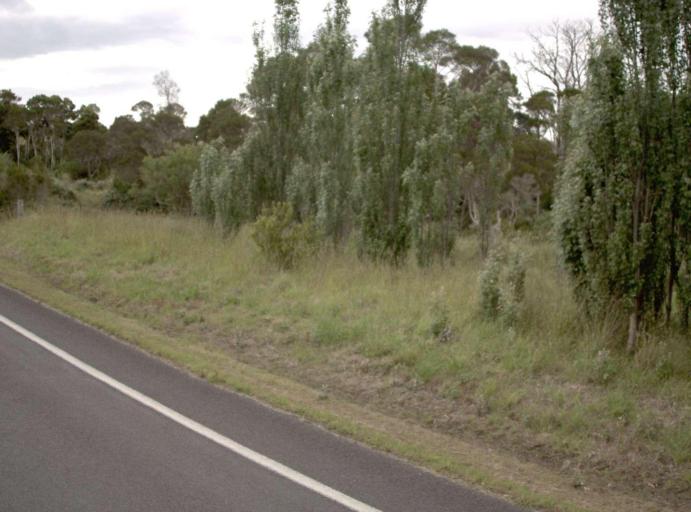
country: AU
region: Victoria
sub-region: Wellington
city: Sale
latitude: -38.2931
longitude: 147.0340
